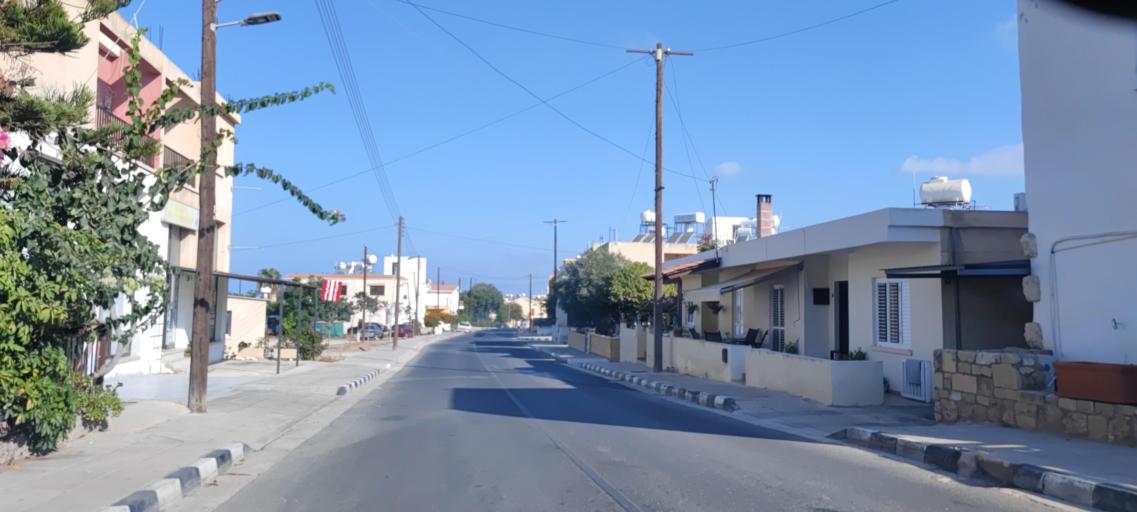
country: CY
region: Pafos
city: Chlorakas
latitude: 34.7954
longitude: 32.4104
